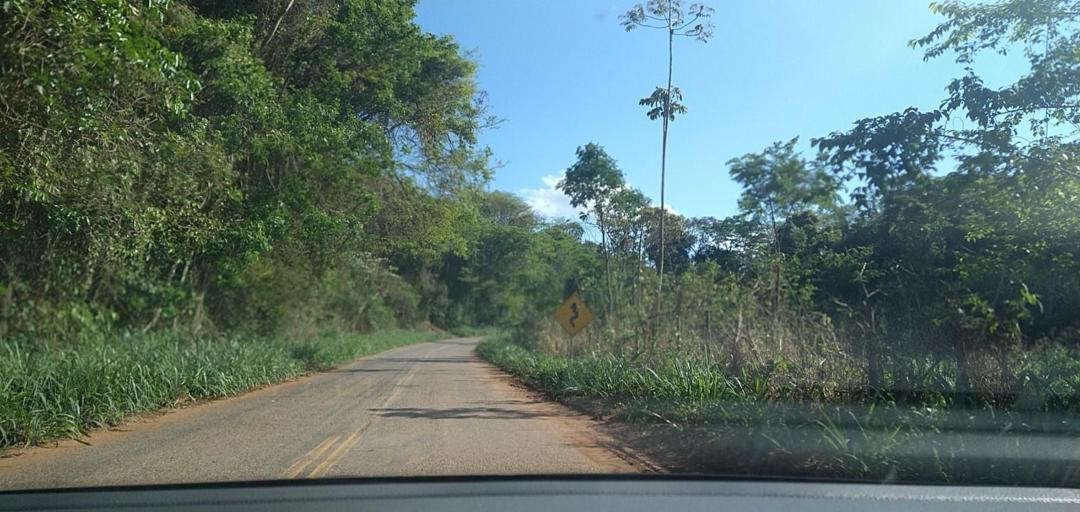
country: BR
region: Minas Gerais
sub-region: Alvinopolis
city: Alvinopolis
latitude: -20.1798
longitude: -42.9312
